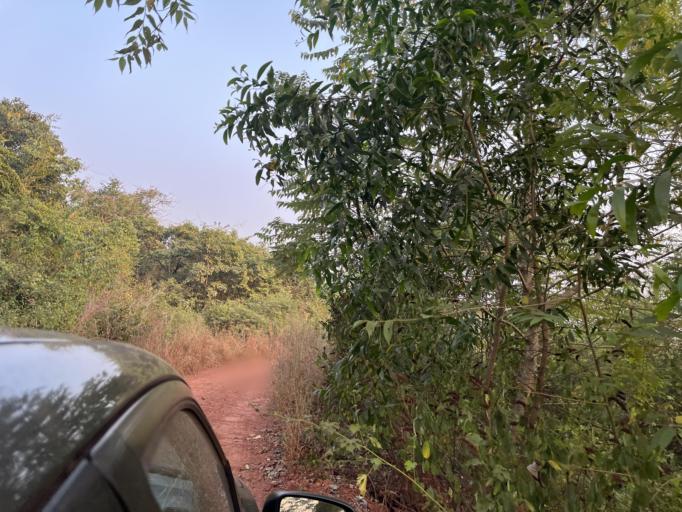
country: IN
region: Goa
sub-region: North Goa
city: Pernem
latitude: 15.7015
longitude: 73.8320
